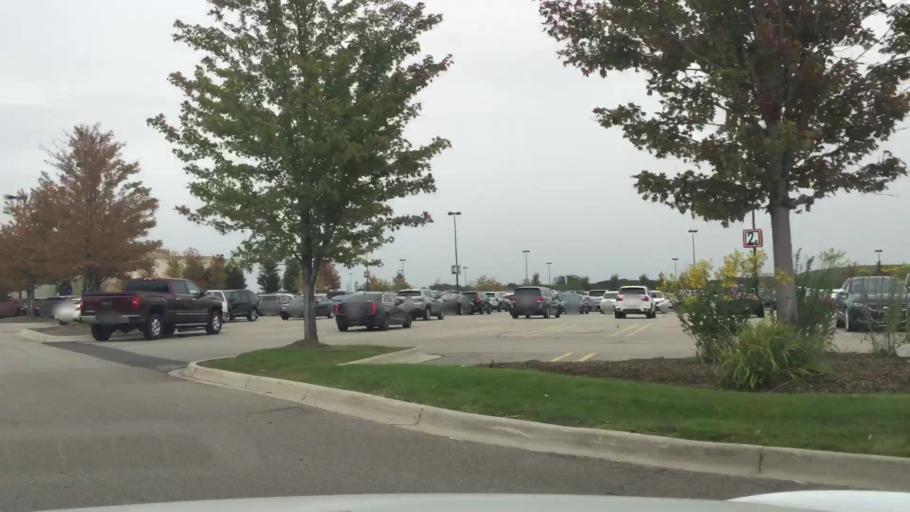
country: US
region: Michigan
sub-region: Oakland County
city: Pontiac
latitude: 42.7015
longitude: -83.3046
